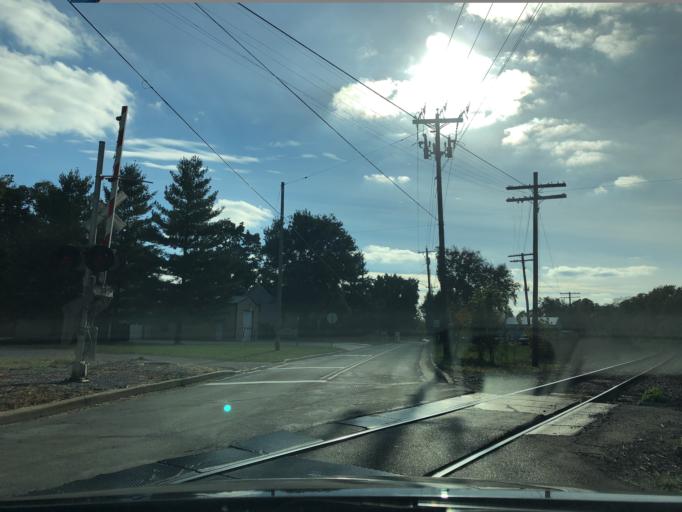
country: US
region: Ohio
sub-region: Hamilton County
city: Loveland
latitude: 39.2665
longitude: -84.2617
